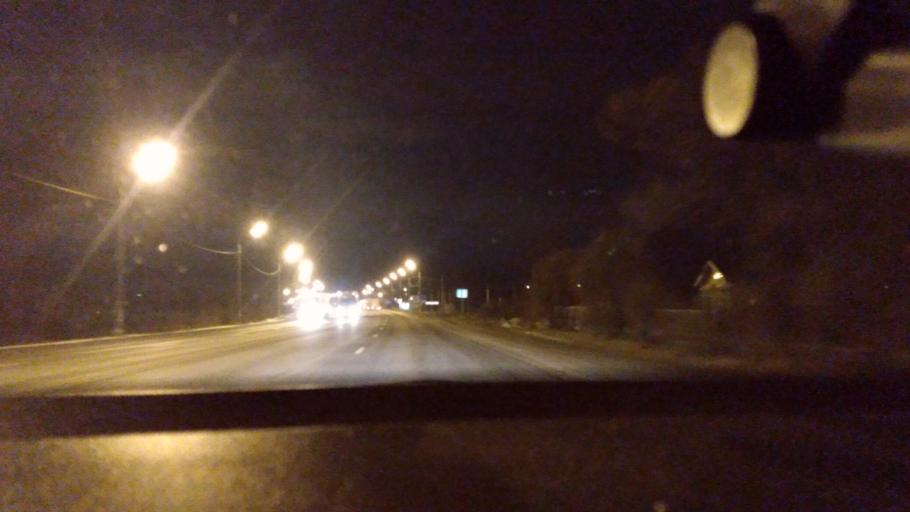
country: RU
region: Moskovskaya
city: Troitskoye
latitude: 55.2753
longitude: 38.4959
